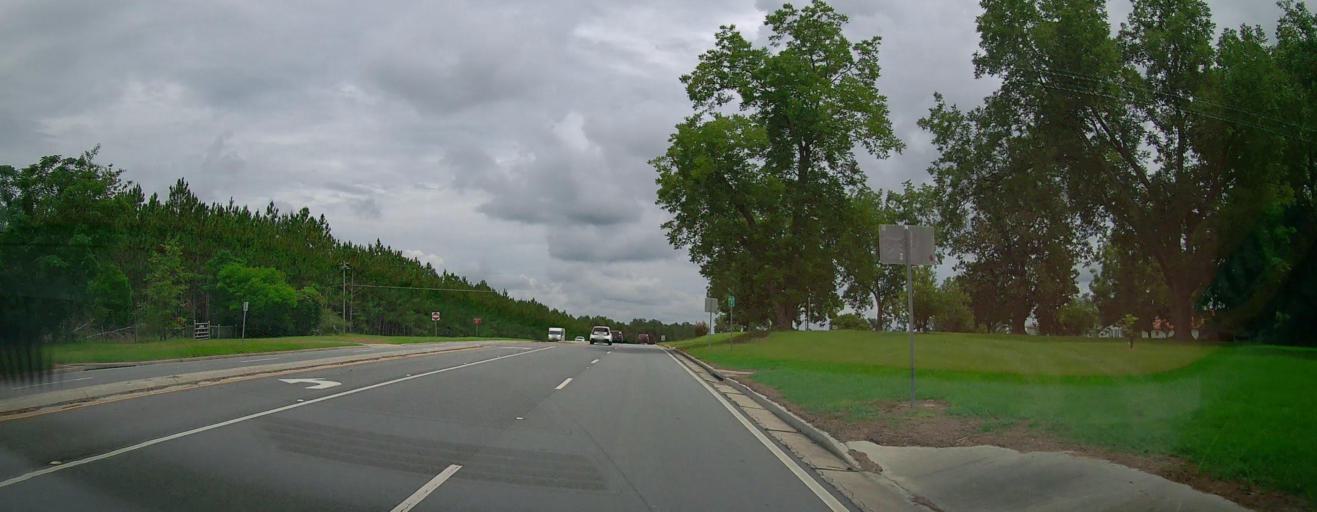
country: US
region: Georgia
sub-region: Telfair County
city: McRae
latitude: 32.0556
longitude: -82.8651
